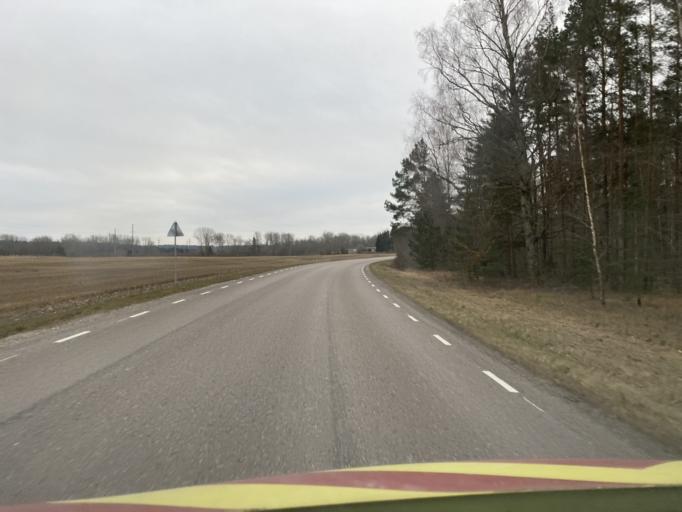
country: EE
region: Laeaene
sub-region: Ridala Parish
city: Uuemoisa
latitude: 59.0267
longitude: 23.6638
